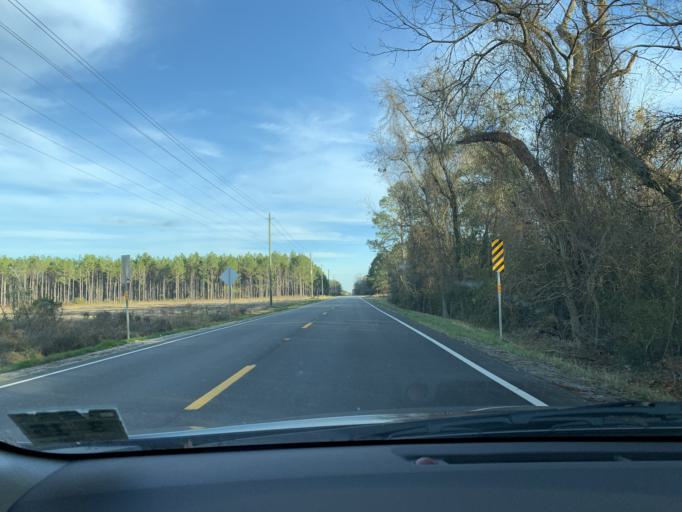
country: US
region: Georgia
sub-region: Irwin County
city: Ocilla
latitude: 31.5847
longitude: -83.0752
